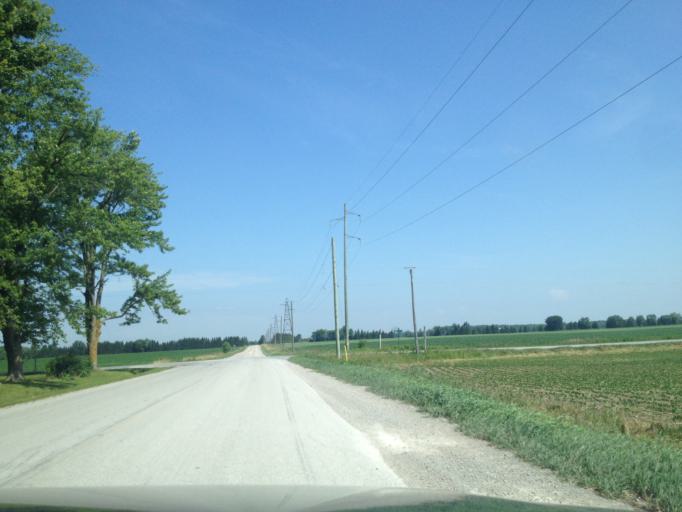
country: CA
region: Ontario
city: London
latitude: 43.1212
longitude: -81.2352
